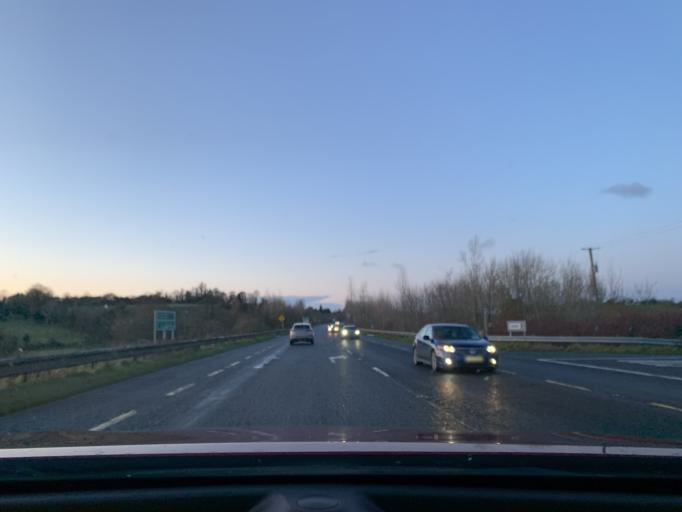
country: IE
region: Connaught
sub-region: County Leitrim
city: Carrick-on-Shannon
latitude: 53.9243
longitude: -7.9947
